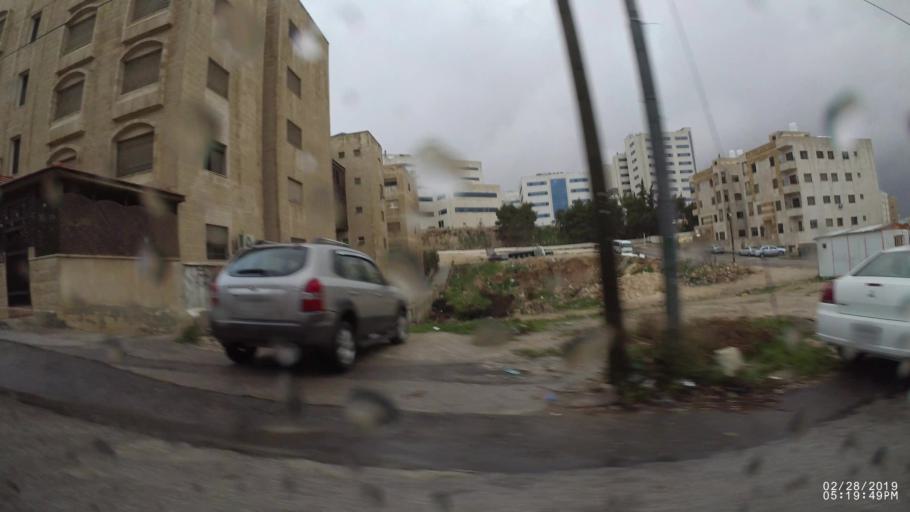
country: JO
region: Amman
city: Amman
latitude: 31.9993
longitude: 35.9207
